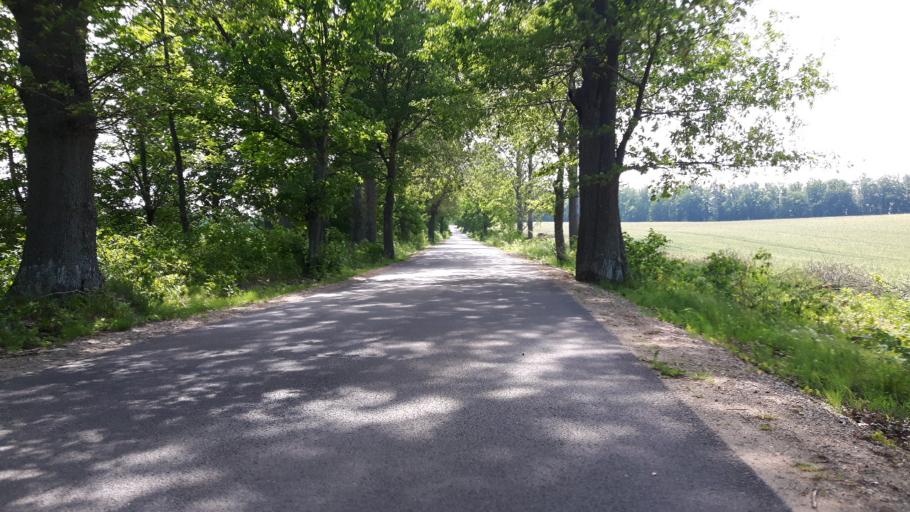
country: PL
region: Pomeranian Voivodeship
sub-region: Powiat wejherowski
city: Choczewo
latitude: 54.7528
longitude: 17.7926
